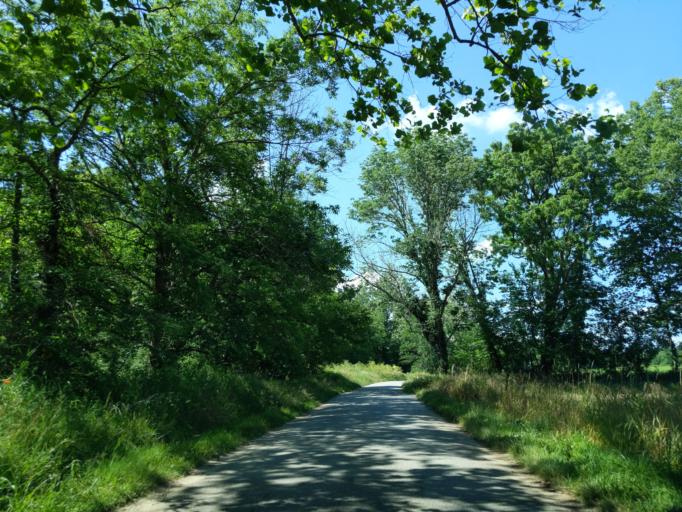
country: US
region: Indiana
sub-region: Ripley County
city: Osgood
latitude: 39.2038
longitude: -85.4158
